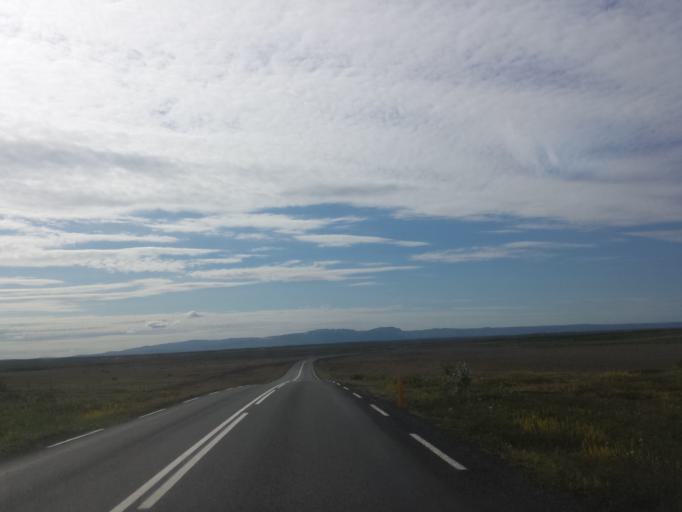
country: IS
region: Northeast
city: Husavik
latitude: 66.0304
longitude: -16.5027
